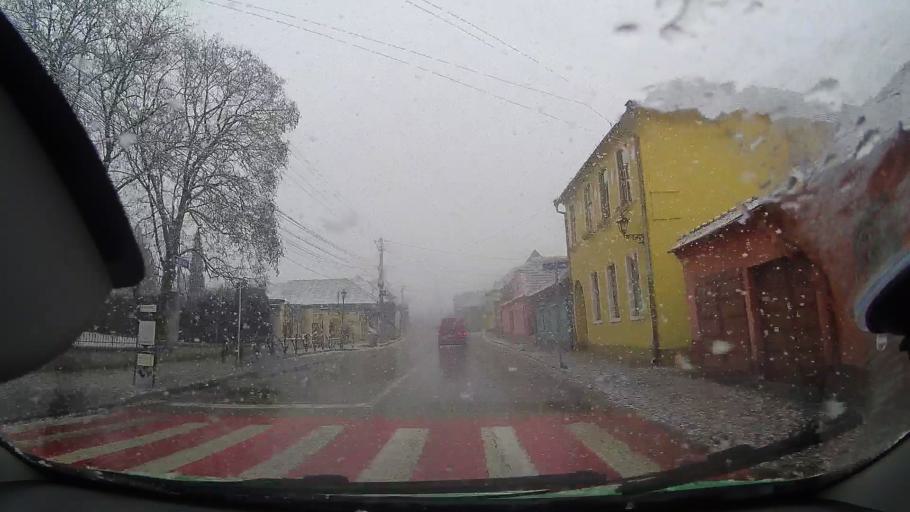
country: RO
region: Sibiu
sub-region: Municipiul Medias
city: Medias
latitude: 46.1687
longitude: 24.3519
